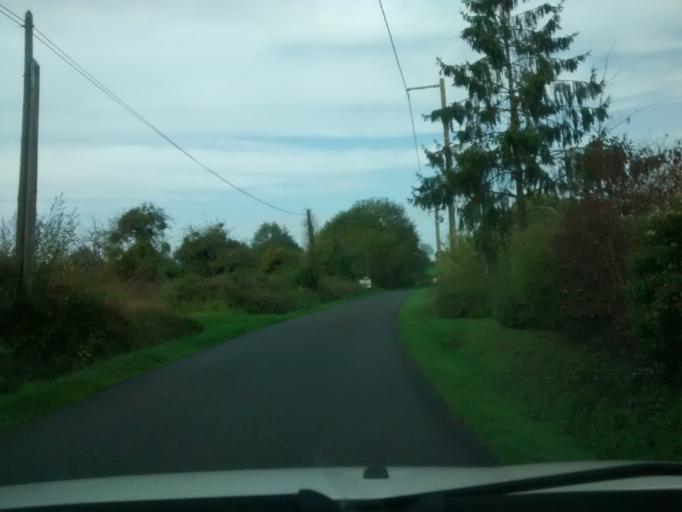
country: FR
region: Brittany
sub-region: Departement d'Ille-et-Vilaine
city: Brece
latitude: 48.1130
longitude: -1.4861
